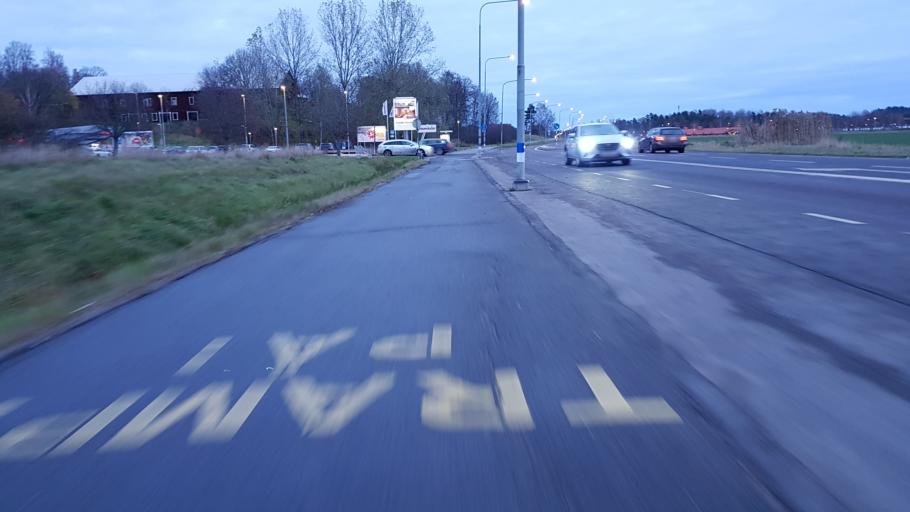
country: SE
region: OEstergoetland
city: Lindo
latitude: 58.6007
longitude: 16.2449
